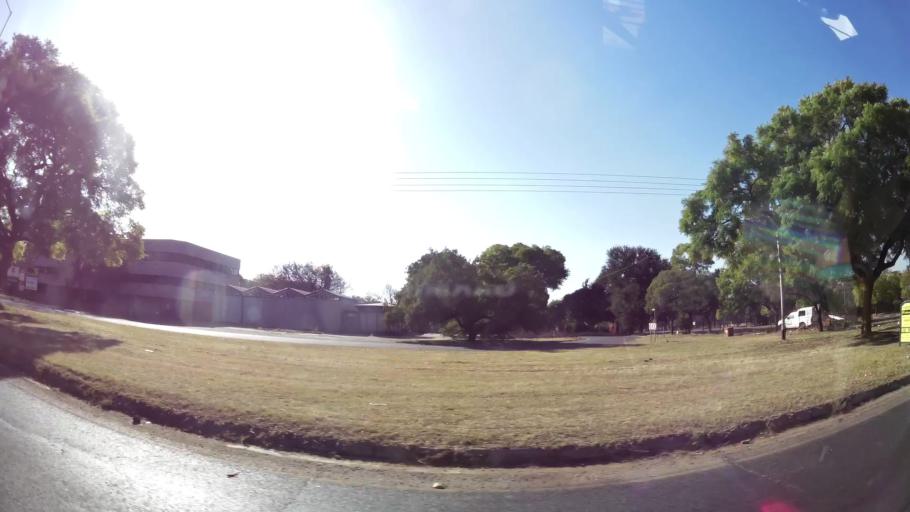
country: ZA
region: Gauteng
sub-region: City of Tshwane Metropolitan Municipality
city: Pretoria
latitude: -25.7323
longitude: 28.2583
